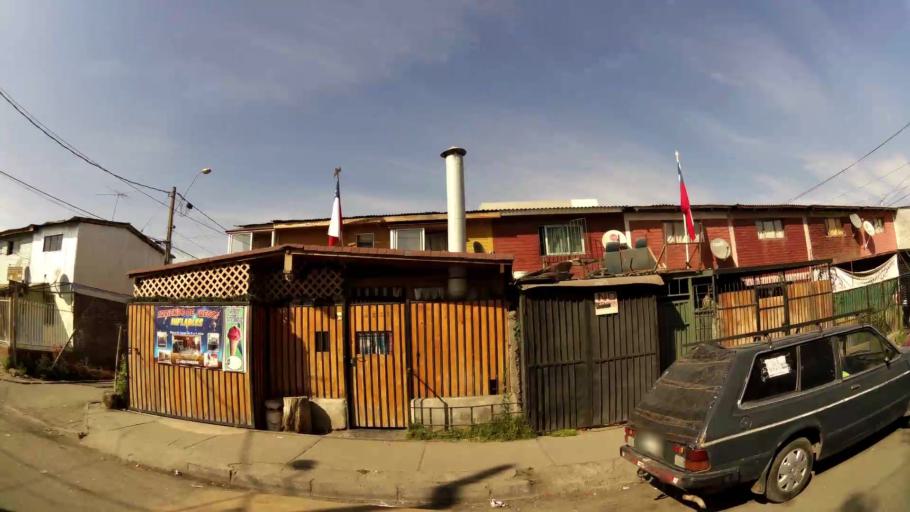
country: CL
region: Santiago Metropolitan
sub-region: Provincia de Santiago
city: La Pintana
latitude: -33.5633
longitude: -70.6359
